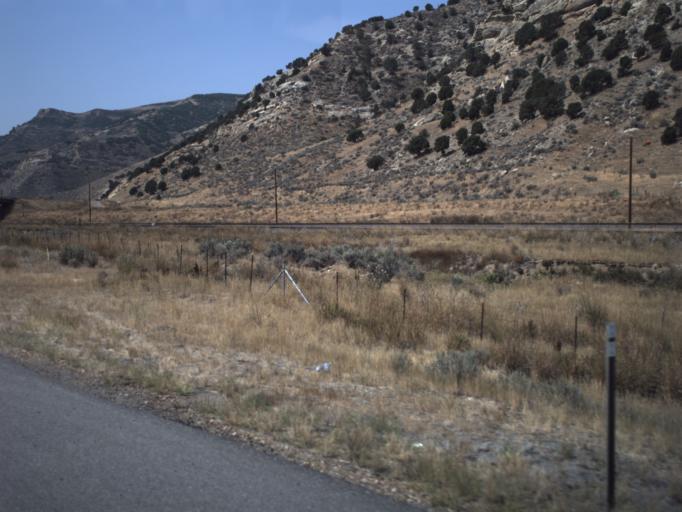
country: US
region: Utah
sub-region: Summit County
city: Coalville
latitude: 41.0688
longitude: -111.2670
